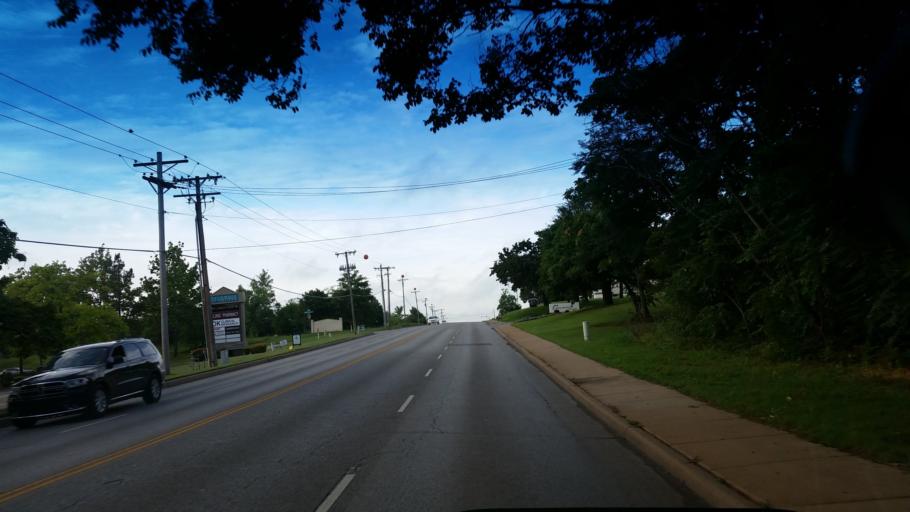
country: US
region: Oklahoma
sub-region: Oklahoma County
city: Edmond
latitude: 35.6563
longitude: -97.4605
